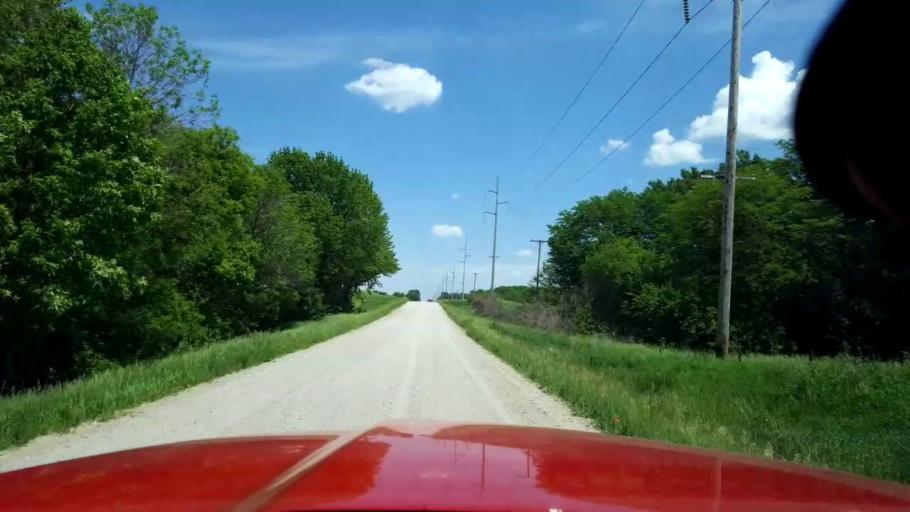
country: US
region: Iowa
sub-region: Story County
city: Gilbert
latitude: 42.0492
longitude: -93.7561
